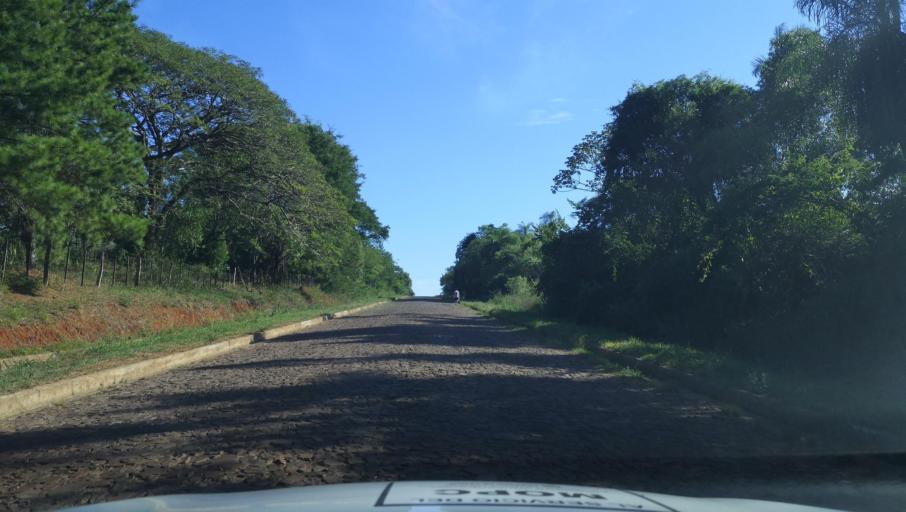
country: PY
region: Misiones
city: Santa Maria
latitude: -26.8805
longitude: -57.0132
